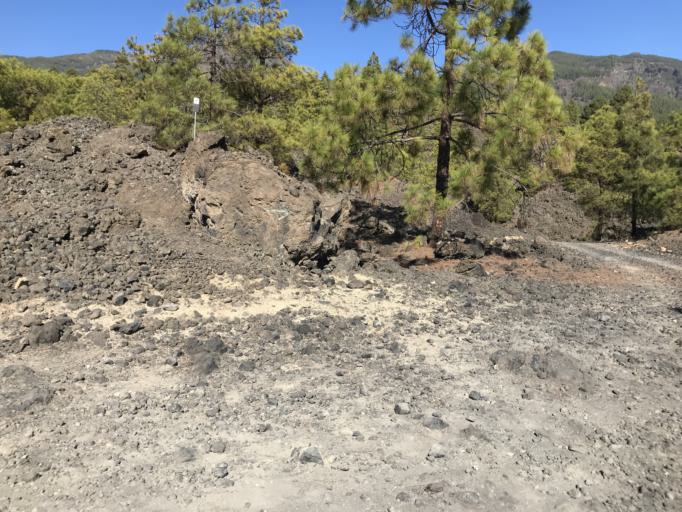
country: ES
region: Canary Islands
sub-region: Provincia de Santa Cruz de Tenerife
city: Arafo
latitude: 28.3320
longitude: -16.4317
